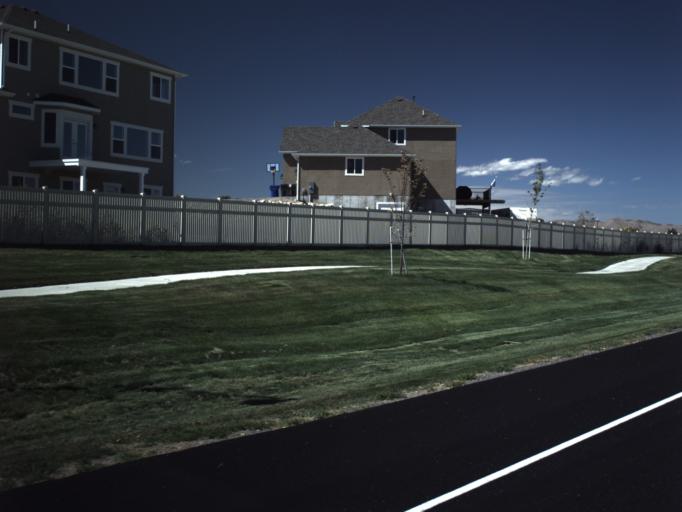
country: US
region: Utah
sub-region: Utah County
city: Saratoga Springs
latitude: 40.3023
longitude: -111.8852
